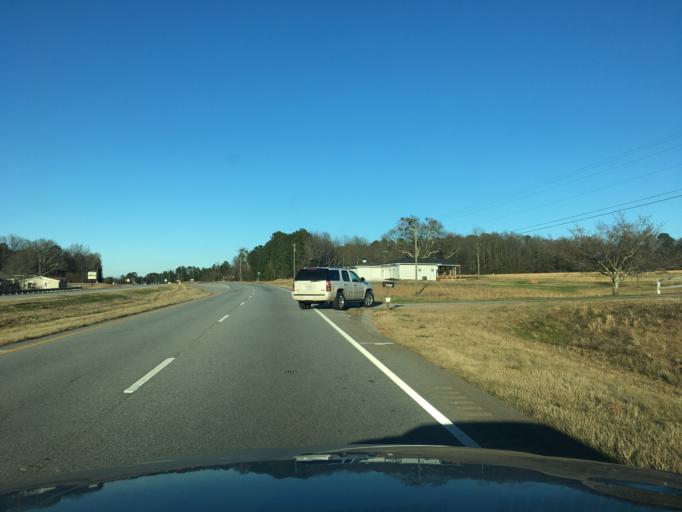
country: US
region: Georgia
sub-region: Carroll County
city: Carrollton
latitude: 33.4993
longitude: -85.0827
